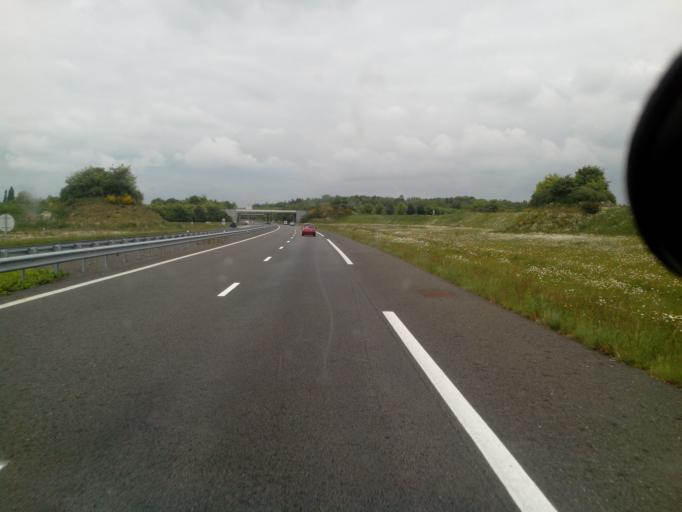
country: FR
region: Brittany
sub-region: Departement d'Ille-et-Vilaine
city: Saint-Sauveur-des-Landes
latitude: 48.3374
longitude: -1.2984
